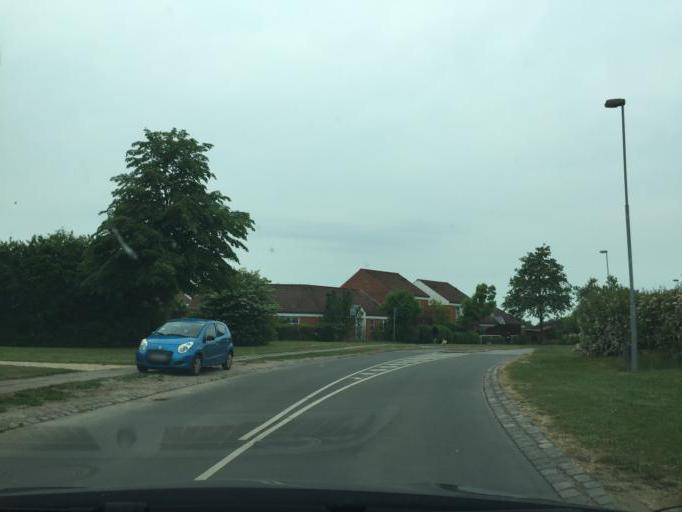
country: DK
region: South Denmark
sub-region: Odense Kommune
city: Neder Holluf
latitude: 55.3620
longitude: 10.4728
